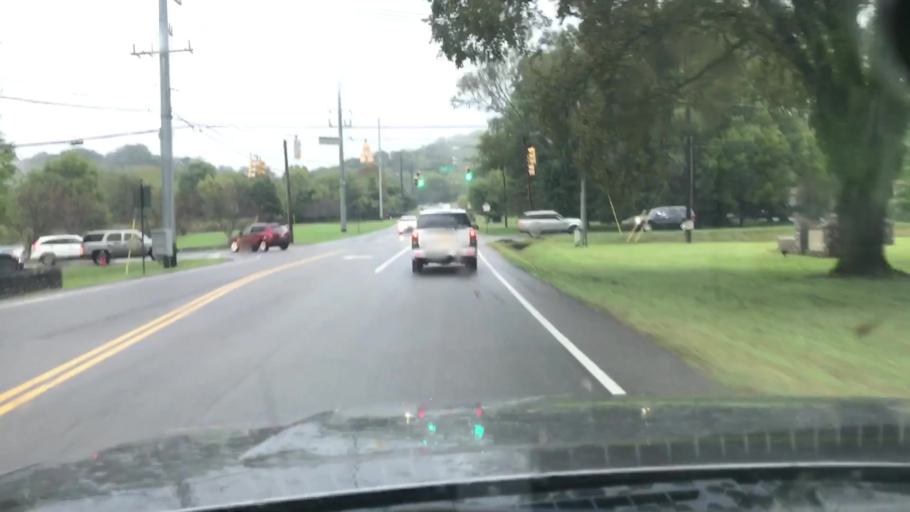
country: US
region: Tennessee
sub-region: Davidson County
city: Forest Hills
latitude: 36.0783
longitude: -86.8374
